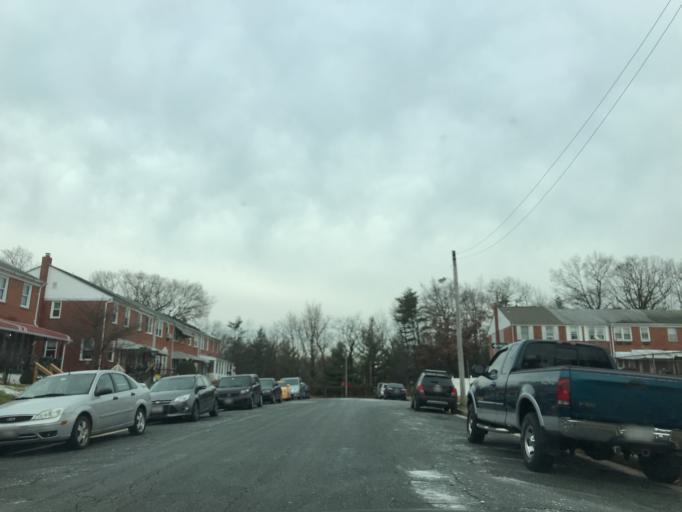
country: US
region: Maryland
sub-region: Baltimore County
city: Essex
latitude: 39.3222
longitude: -76.4597
